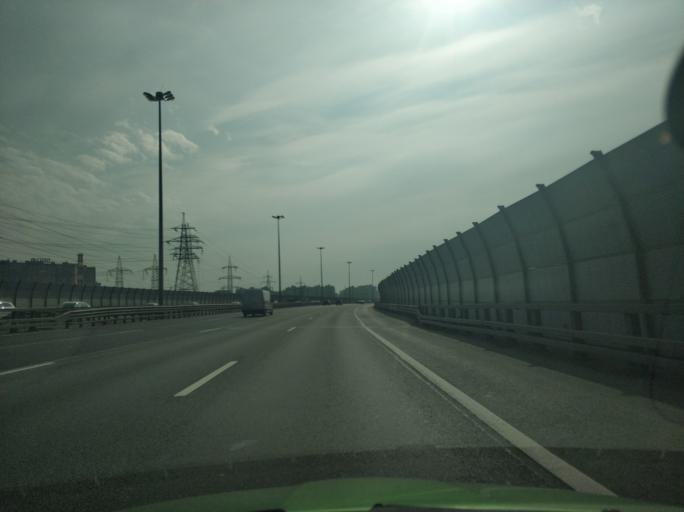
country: RU
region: Leningrad
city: Murino
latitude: 60.0436
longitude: 30.4354
